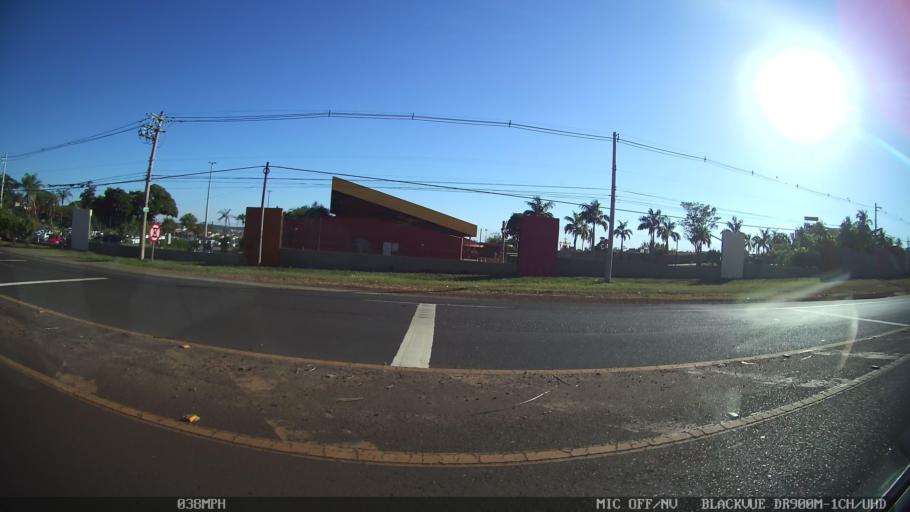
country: BR
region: Sao Paulo
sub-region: Olimpia
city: Olimpia
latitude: -20.7190
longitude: -48.9068
